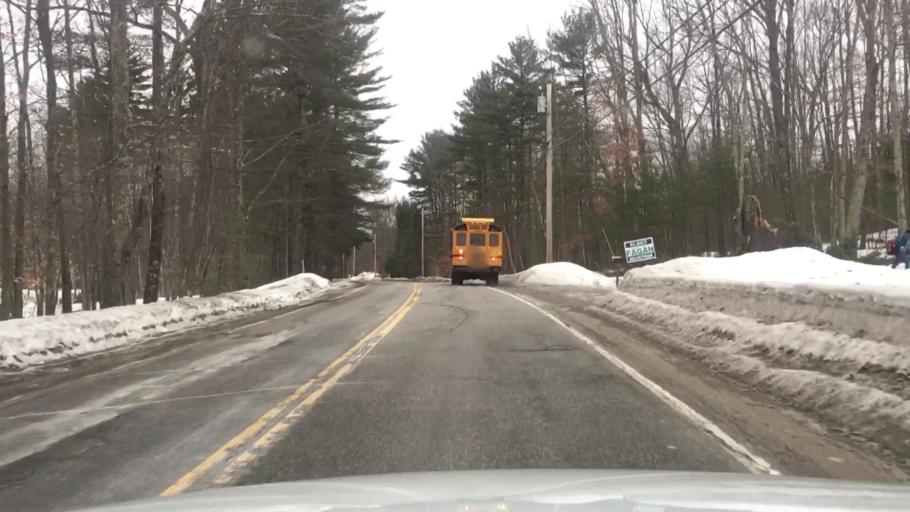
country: US
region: Maine
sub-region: York County
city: Shapleigh
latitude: 43.5518
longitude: -70.8538
